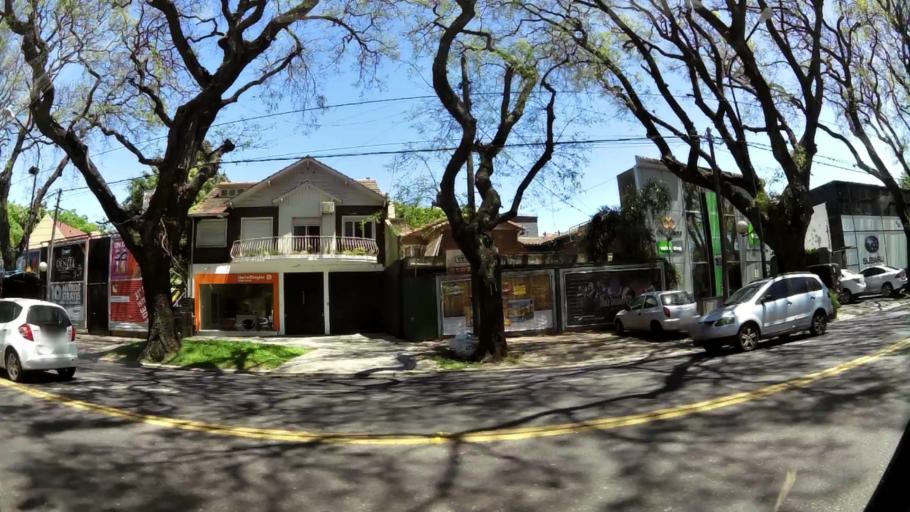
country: AR
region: Buenos Aires
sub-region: Partido de Vicente Lopez
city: Olivos
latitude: -34.4895
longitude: -58.4850
